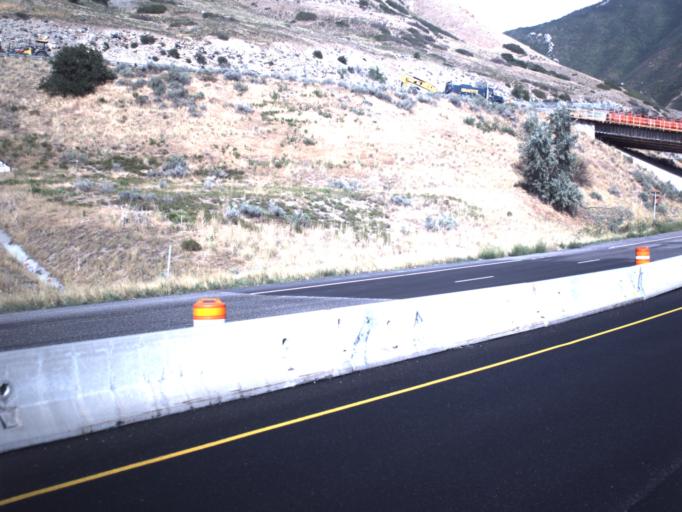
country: US
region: Utah
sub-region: Salt Lake County
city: East Millcreek
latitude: 40.7122
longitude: -111.8065
